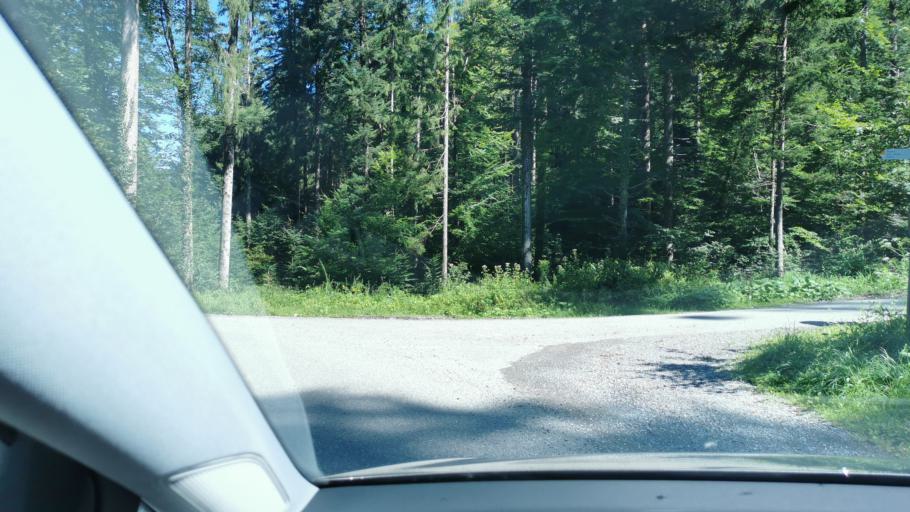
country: AT
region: Vorarlberg
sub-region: Politischer Bezirk Feldkirch
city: Viktorsberg
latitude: 47.2859
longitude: 9.6730
